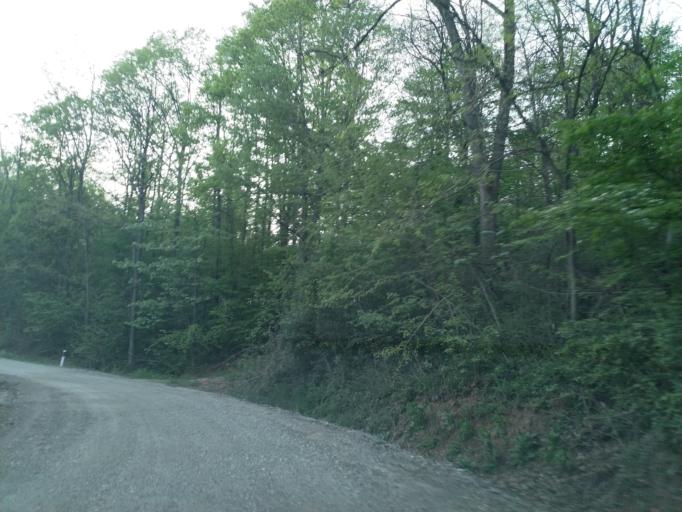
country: RS
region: Central Serbia
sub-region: Pomoravski Okrug
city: Despotovac
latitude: 43.9623
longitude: 21.5614
